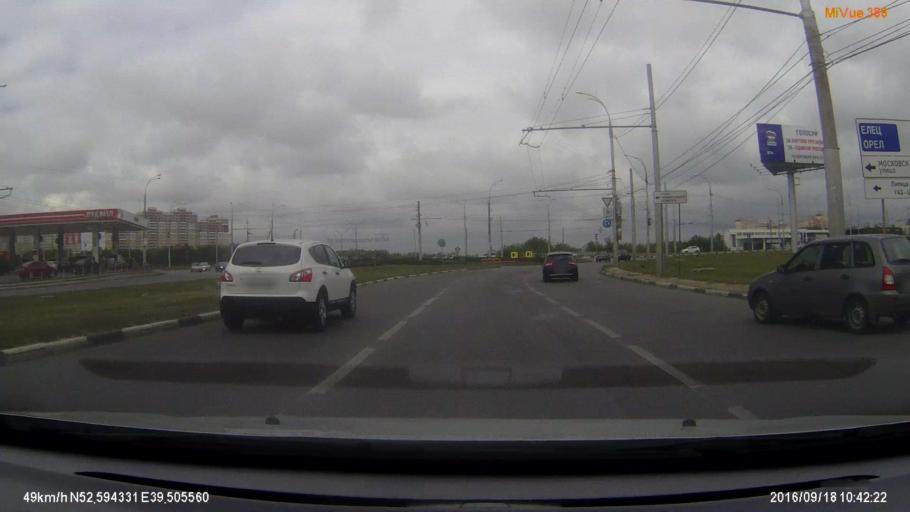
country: RU
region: Lipetsk
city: Syrskoye
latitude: 52.5941
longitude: 39.5060
